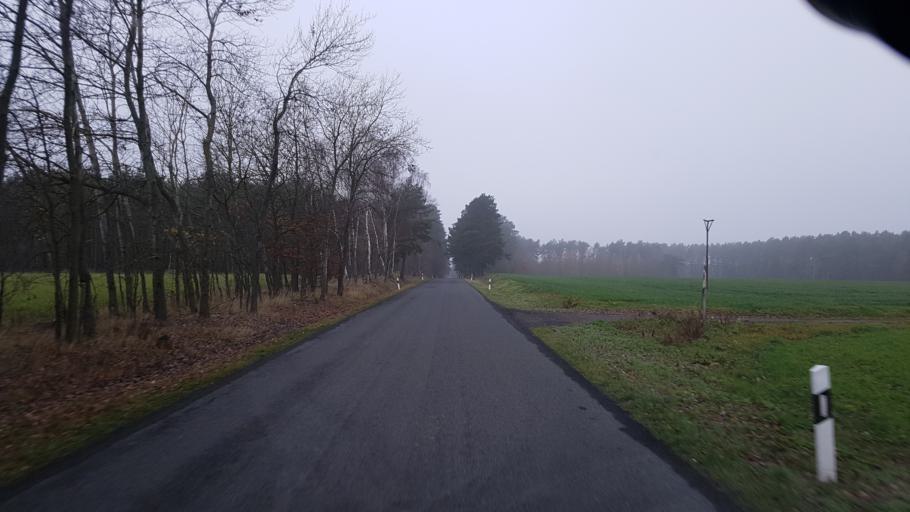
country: DE
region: Brandenburg
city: Bronkow
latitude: 51.6869
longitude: 13.9386
